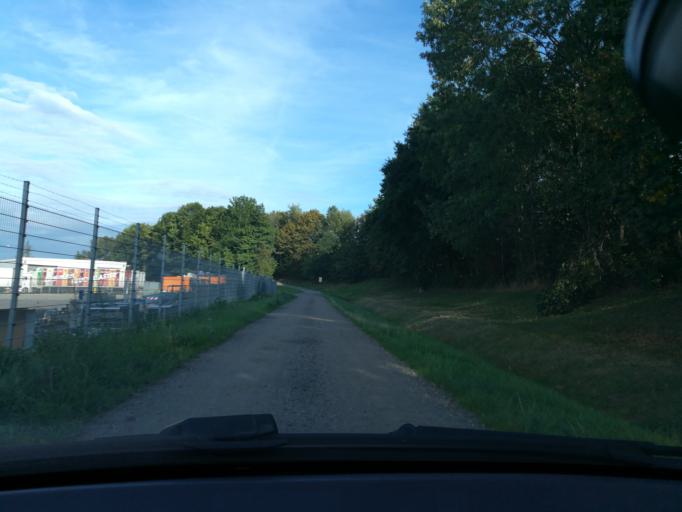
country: DE
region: North Rhine-Westphalia
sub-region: Regierungsbezirk Detmold
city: Minden
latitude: 52.3047
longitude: 8.9556
